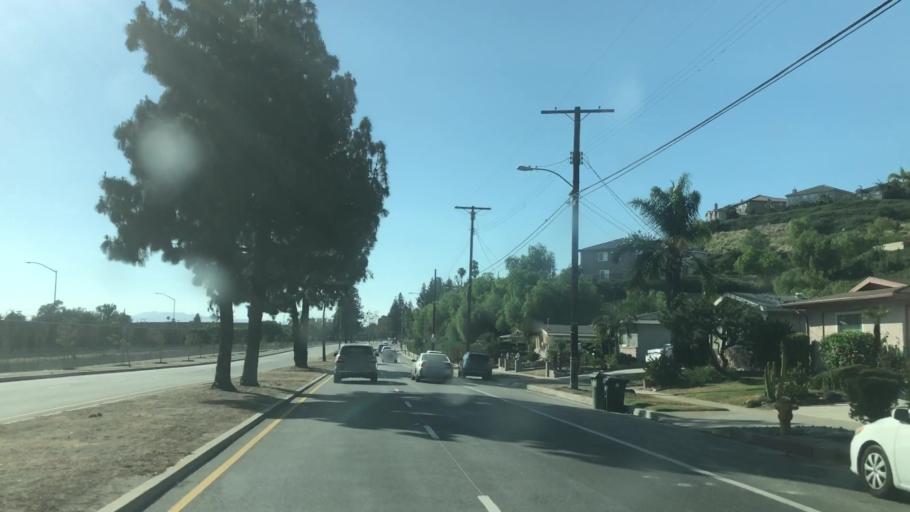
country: US
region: California
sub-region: Los Angeles County
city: North Hollywood
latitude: 34.2146
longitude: -118.3501
